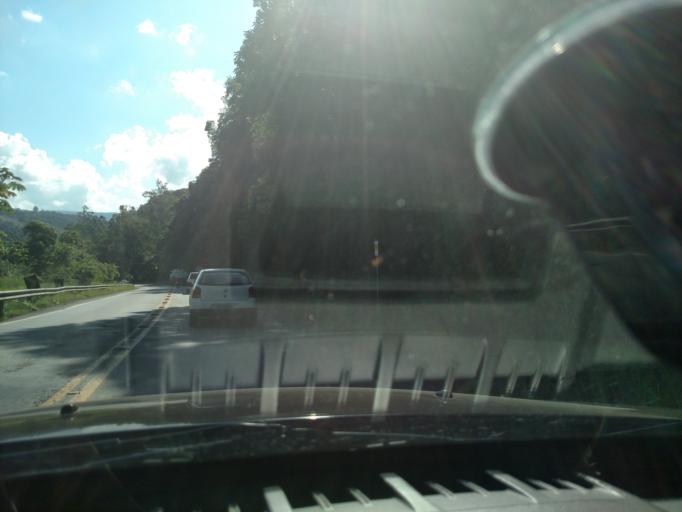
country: BR
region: Santa Catarina
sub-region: Ibirama
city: Ibirama
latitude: -27.0820
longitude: -49.5056
